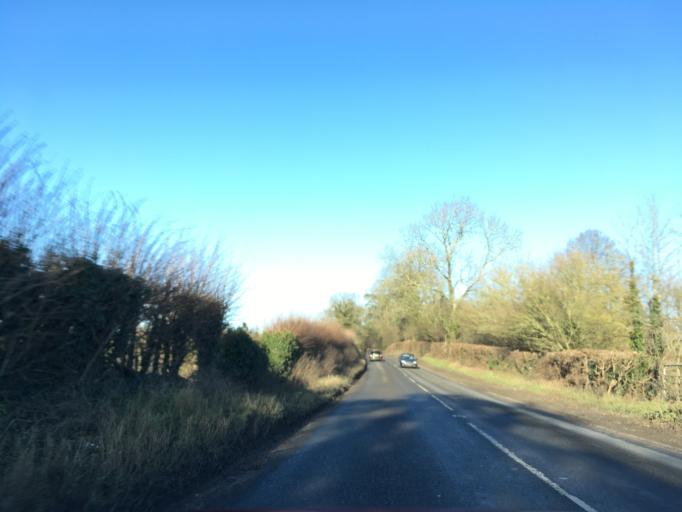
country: GB
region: England
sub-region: Wiltshire
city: Chippenham
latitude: 51.4784
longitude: -2.1052
